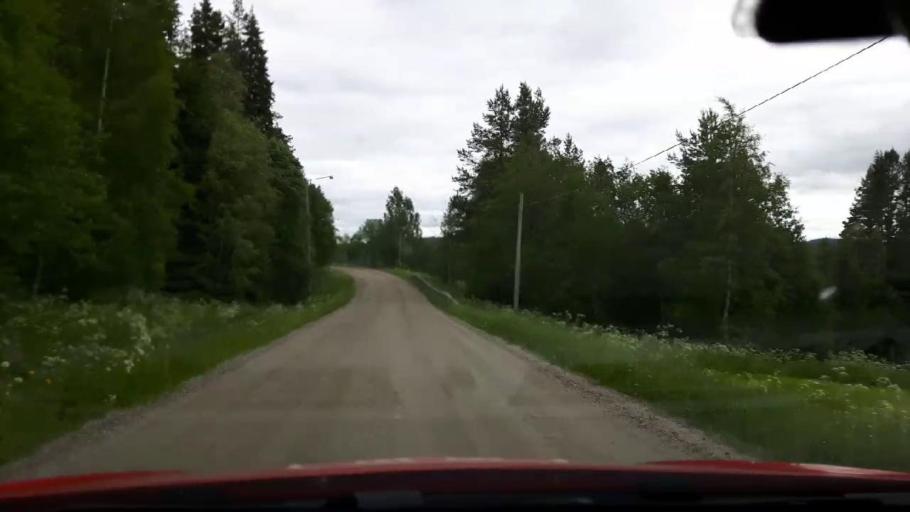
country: SE
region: Jaemtland
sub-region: Ragunda Kommun
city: Hammarstrand
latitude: 63.1699
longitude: 16.2049
